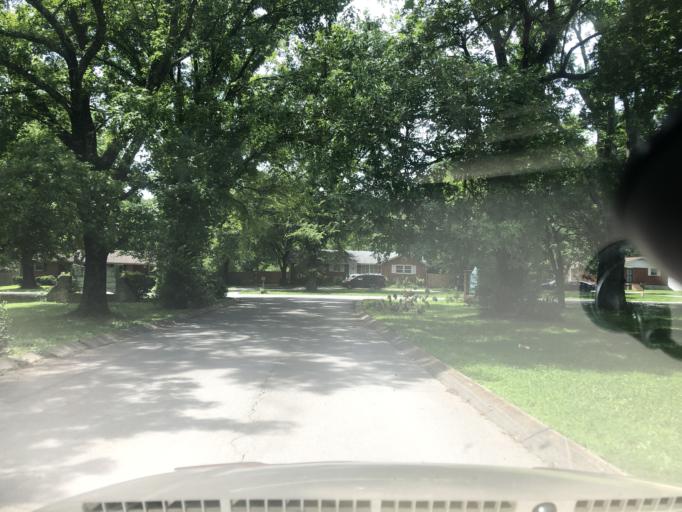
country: US
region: Tennessee
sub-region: Davidson County
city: Goodlettsville
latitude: 36.2583
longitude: -86.7034
